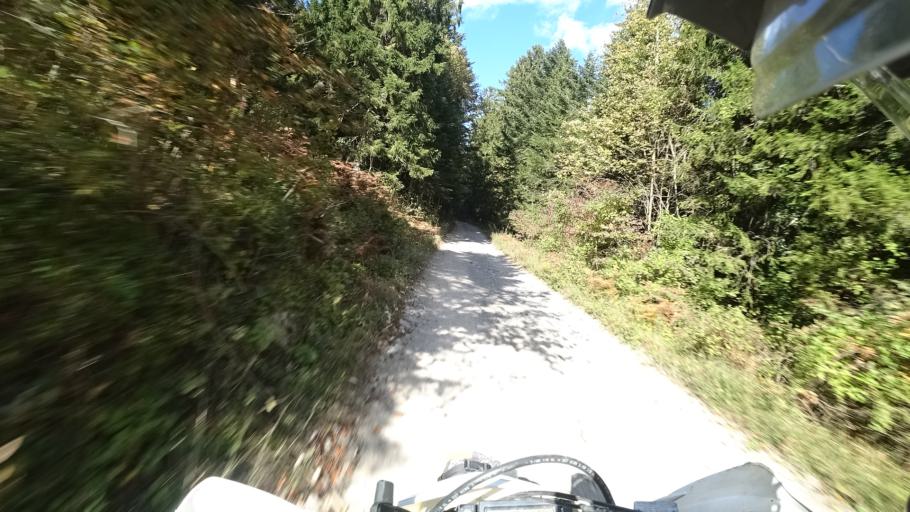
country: HR
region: Karlovacka
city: Plaski
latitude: 45.0676
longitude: 15.3468
